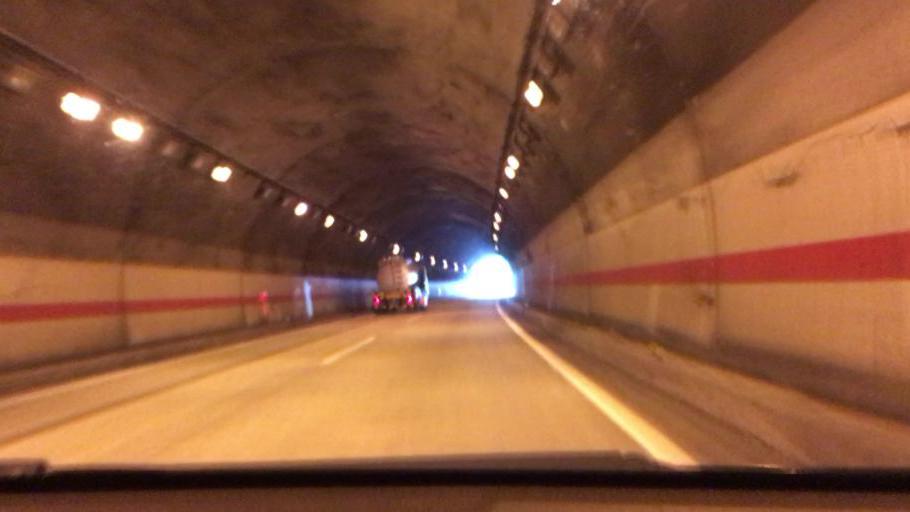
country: JP
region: Yamaguchi
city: Tokuyama
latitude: 34.0667
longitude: 131.6929
